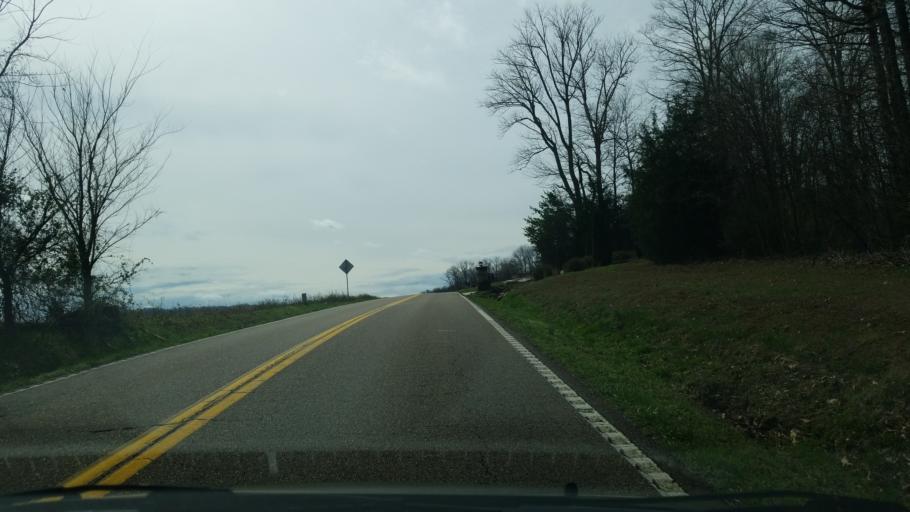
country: US
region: Tennessee
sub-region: Hamilton County
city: Collegedale
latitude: 35.1026
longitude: -85.0645
